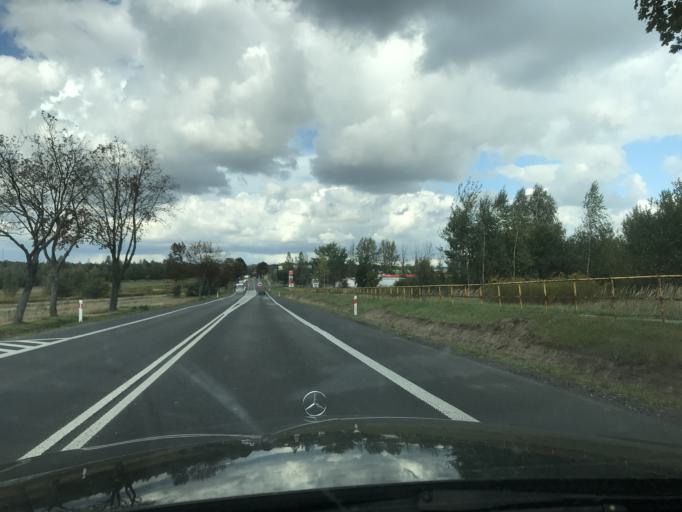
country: PL
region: Lublin Voivodeship
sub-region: Powiat lubelski
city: Niemce
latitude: 51.3682
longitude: 22.6319
